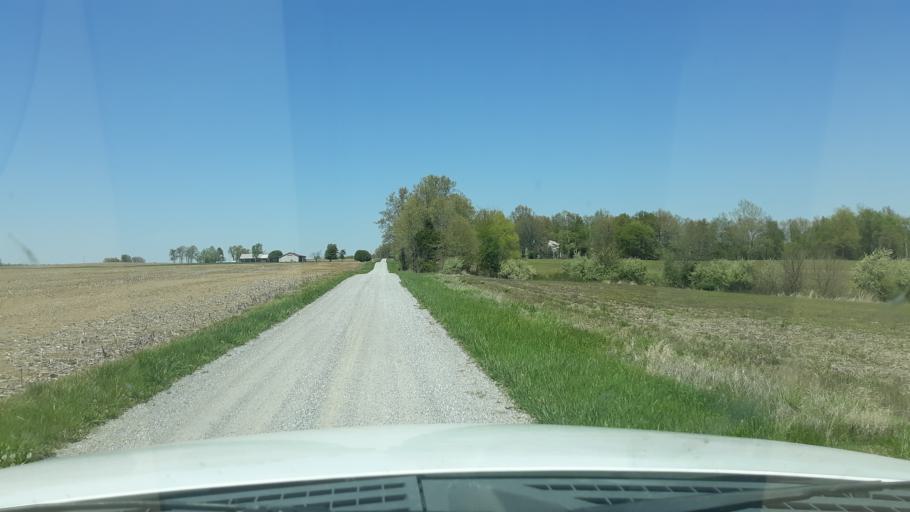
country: US
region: Illinois
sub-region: Saline County
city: Harrisburg
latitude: 37.8781
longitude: -88.6421
